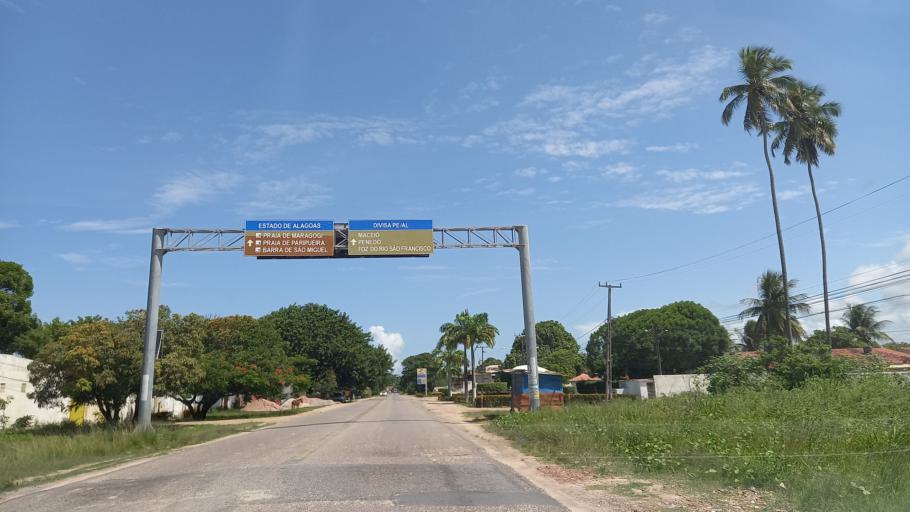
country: BR
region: Pernambuco
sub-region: Sao Jose Da Coroa Grande
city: Sao Jose da Coroa Grande
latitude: -8.9089
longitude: -35.1528
